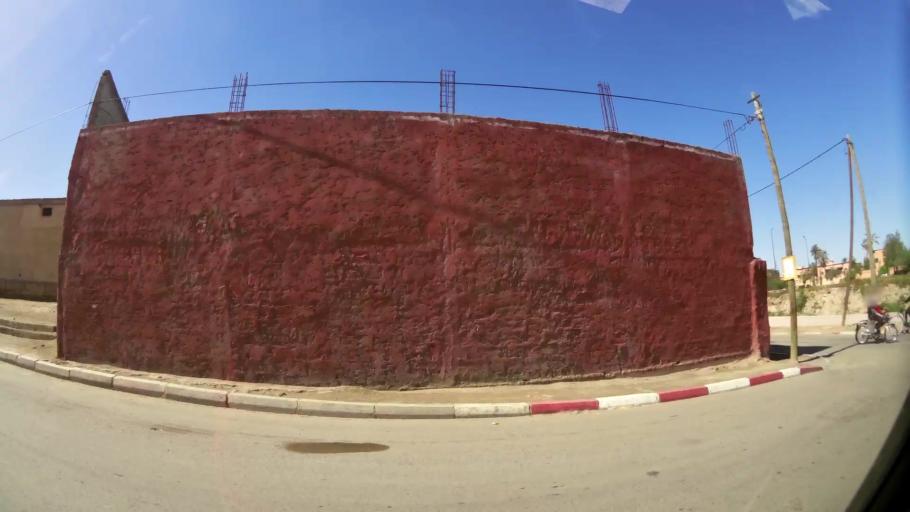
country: MA
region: Marrakech-Tensift-Al Haouz
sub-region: Marrakech
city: Marrakesh
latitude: 31.6499
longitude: -7.9852
